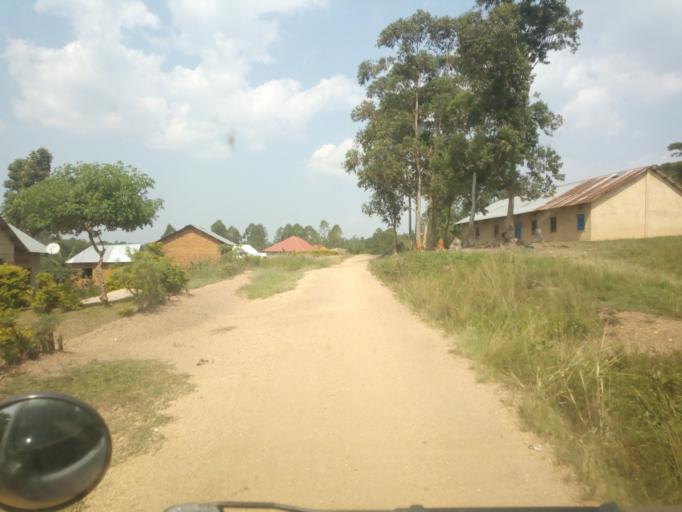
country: UG
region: Western Region
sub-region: Kanungu District
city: Ntungamo
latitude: -0.7920
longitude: 29.6603
